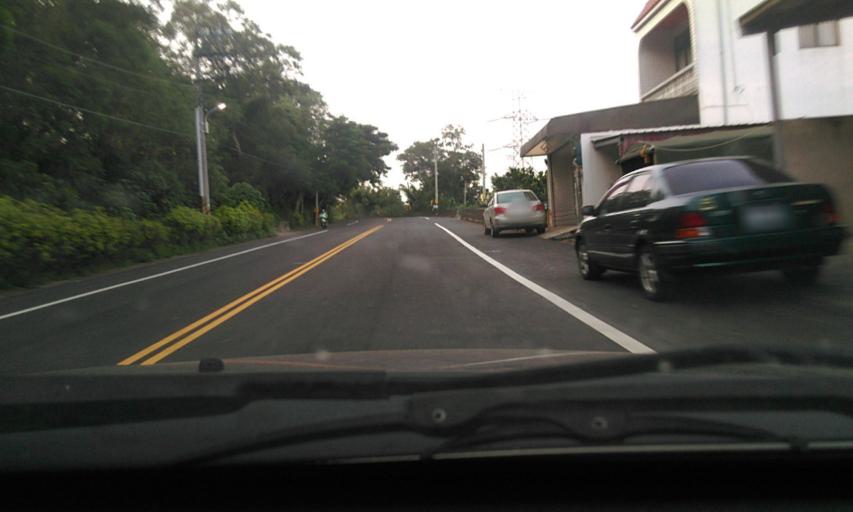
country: TW
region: Taiwan
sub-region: Hsinchu
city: Hsinchu
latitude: 24.6896
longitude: 120.9889
